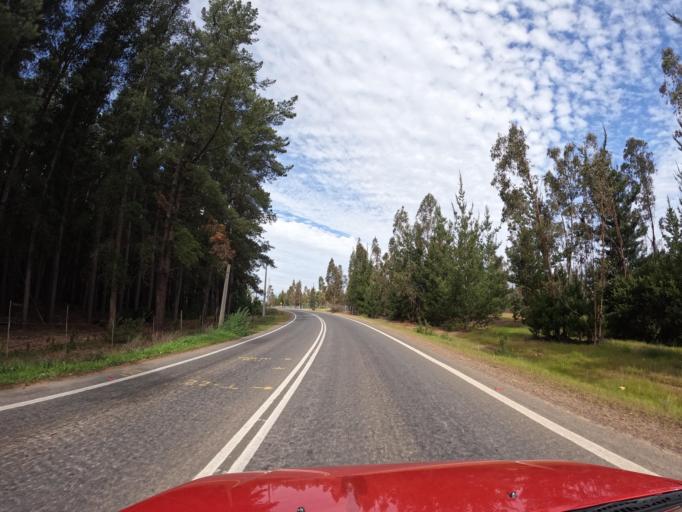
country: CL
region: O'Higgins
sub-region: Provincia de Colchagua
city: Santa Cruz
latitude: -34.2966
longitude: -71.8193
